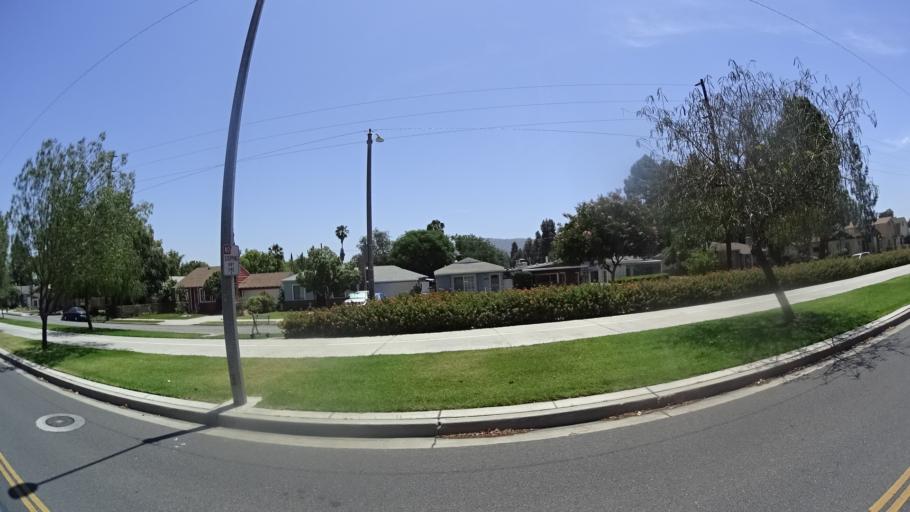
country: US
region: California
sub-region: Los Angeles County
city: Burbank
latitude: 34.1739
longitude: -118.3412
